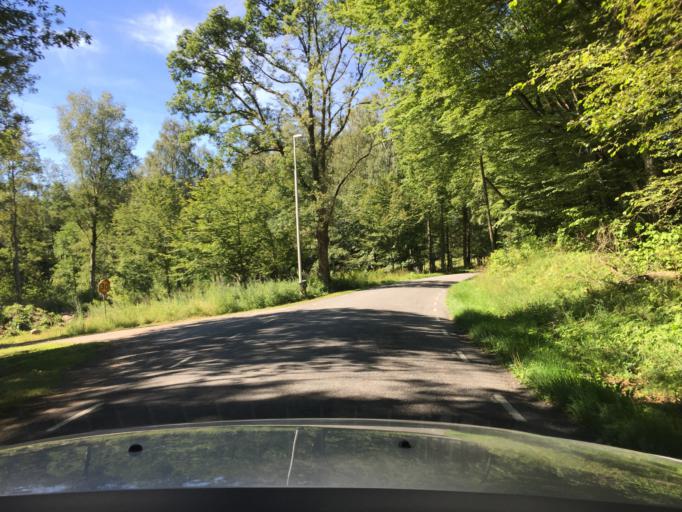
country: SE
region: Skane
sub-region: Hassleholms Kommun
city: Sosdala
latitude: 56.0393
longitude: 13.6568
